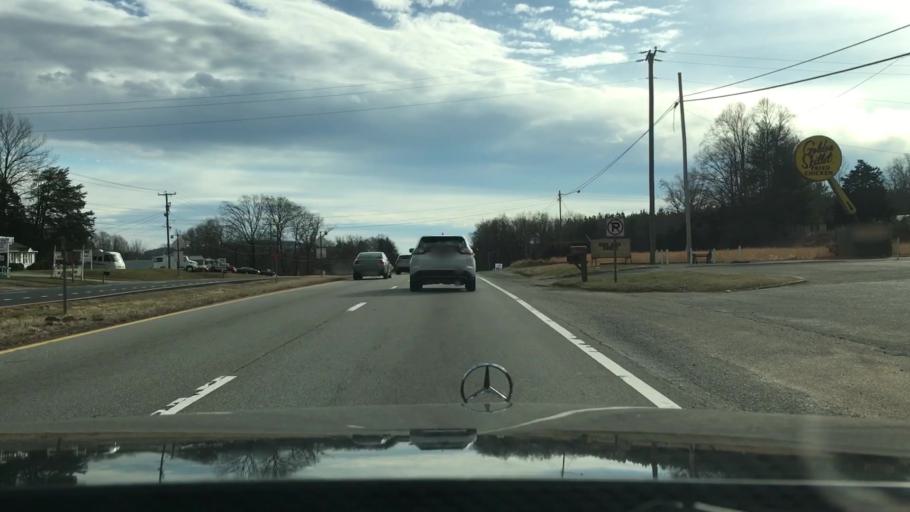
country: US
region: Virginia
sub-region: Pittsylvania County
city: Chatham
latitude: 36.7885
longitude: -79.3941
